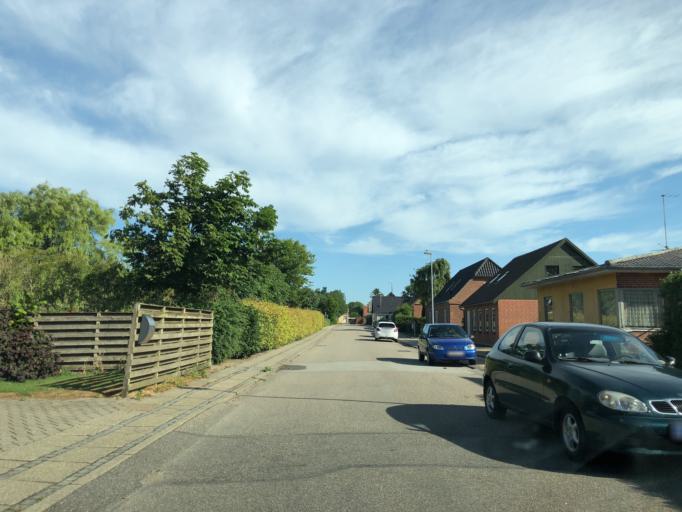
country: DK
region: Central Jutland
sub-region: Holstebro Kommune
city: Ulfborg
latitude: 56.3414
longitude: 8.3419
